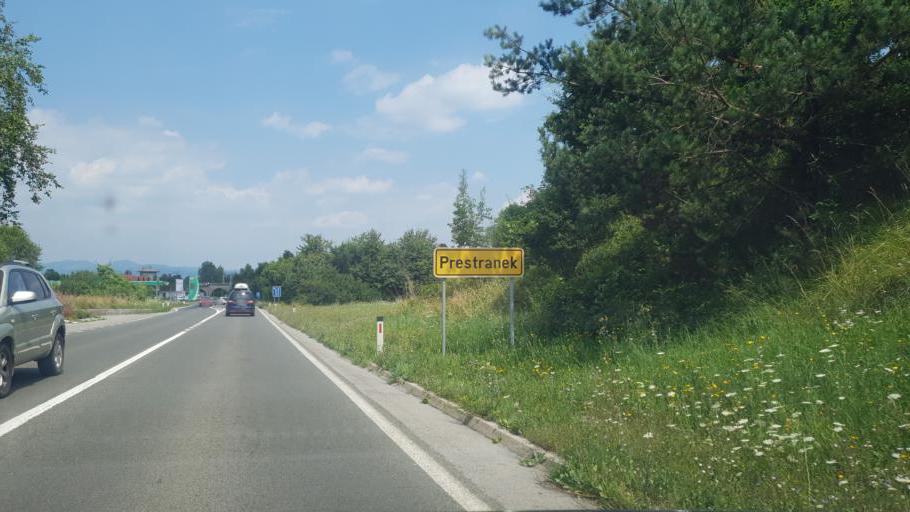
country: SI
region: Pivka
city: Pivka
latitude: 45.7263
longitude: 14.1891
